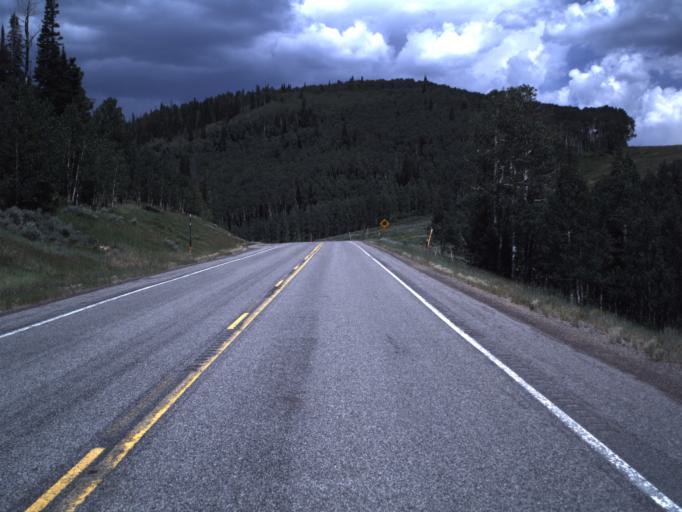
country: US
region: Utah
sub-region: Sanpete County
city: Fairview
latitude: 39.5873
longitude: -111.2278
